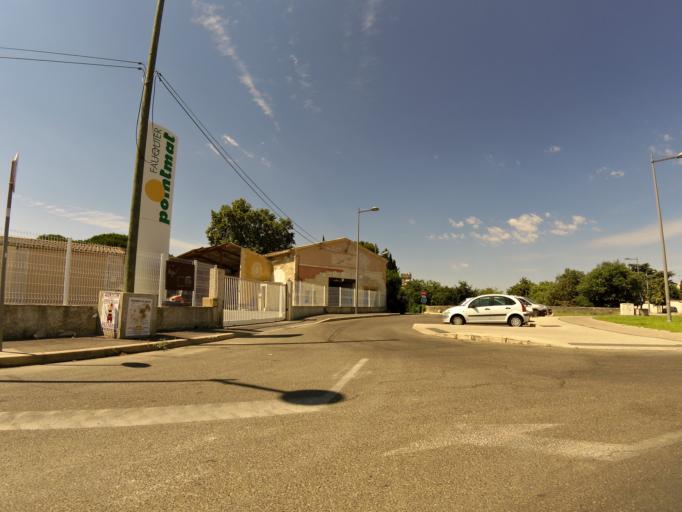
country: FR
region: Languedoc-Roussillon
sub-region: Departement de l'Herault
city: Castelnau-le-Lez
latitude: 43.6338
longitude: 3.9217
